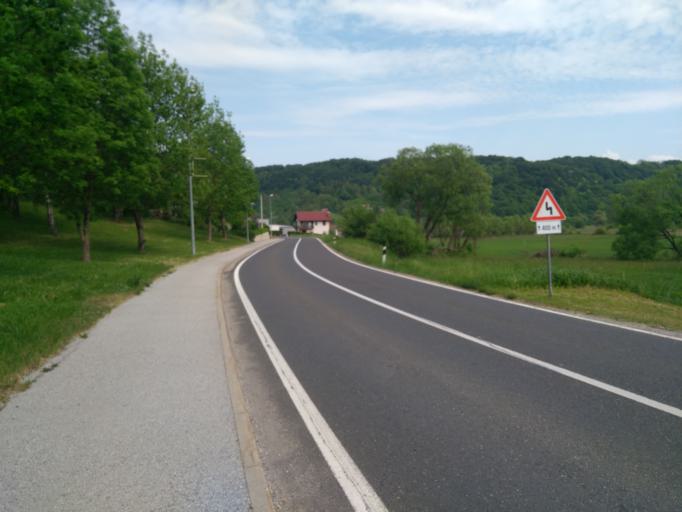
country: HR
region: Varazdinska
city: Lepoglava
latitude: 46.2294
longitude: 15.9842
